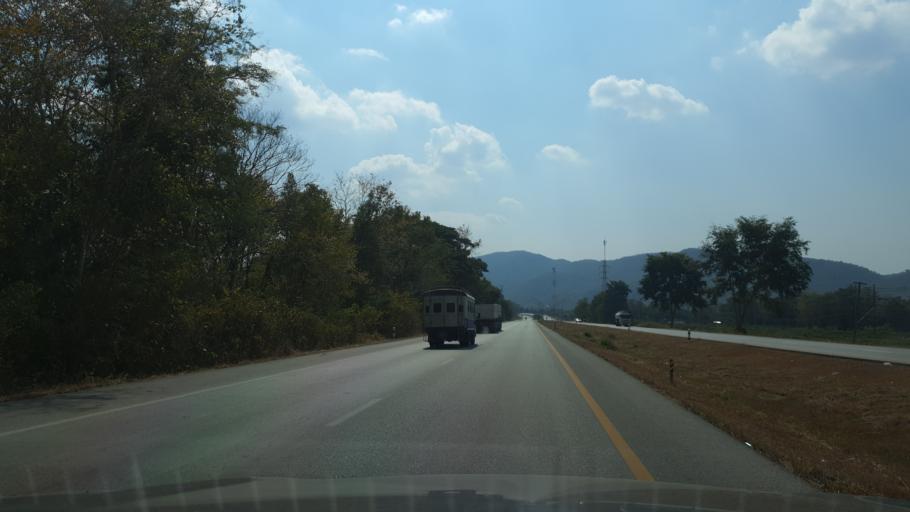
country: TH
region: Lampang
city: Mae Phrik
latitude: 17.3721
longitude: 99.1487
